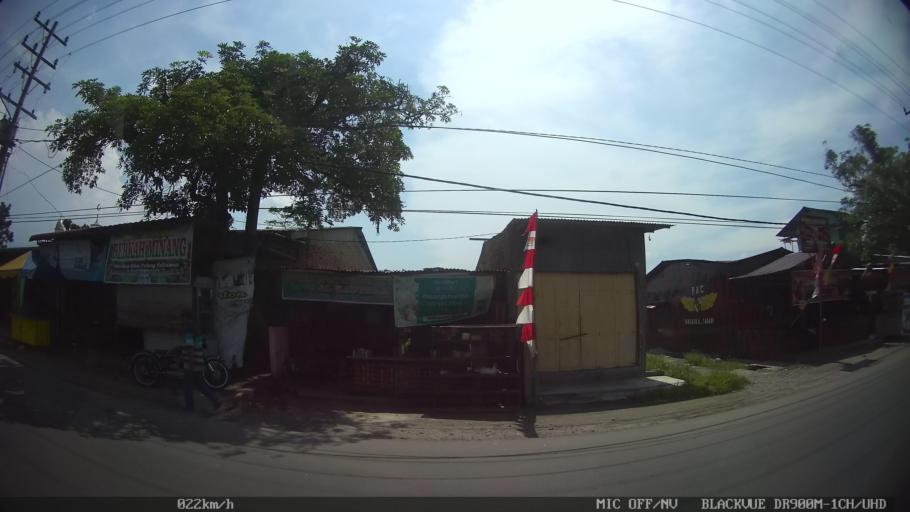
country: ID
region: North Sumatra
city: Medan
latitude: 3.6371
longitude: 98.6586
